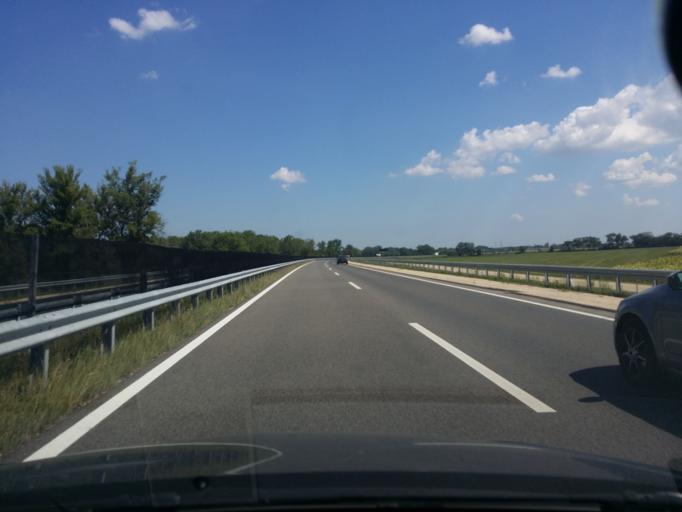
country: HU
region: Gyor-Moson-Sopron
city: Abda
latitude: 47.6676
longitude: 17.5207
